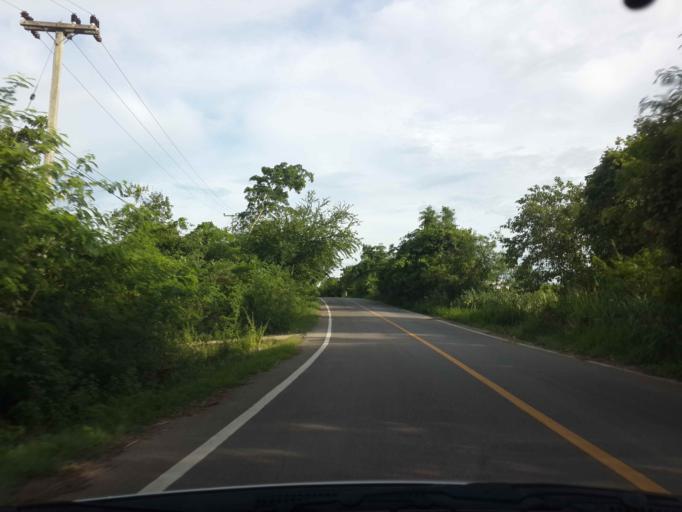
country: TH
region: Kanchanaburi
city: Dan Makham Tia
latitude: 13.8641
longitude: 99.1649
